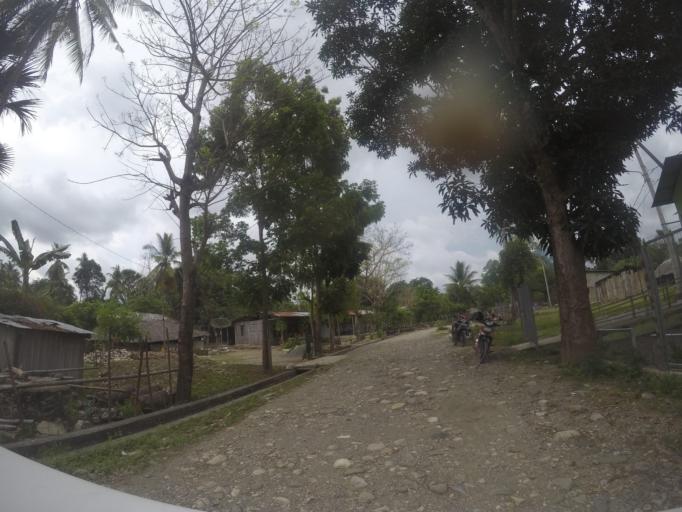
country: TL
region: Viqueque
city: Viqueque
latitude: -8.8802
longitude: 126.3689
